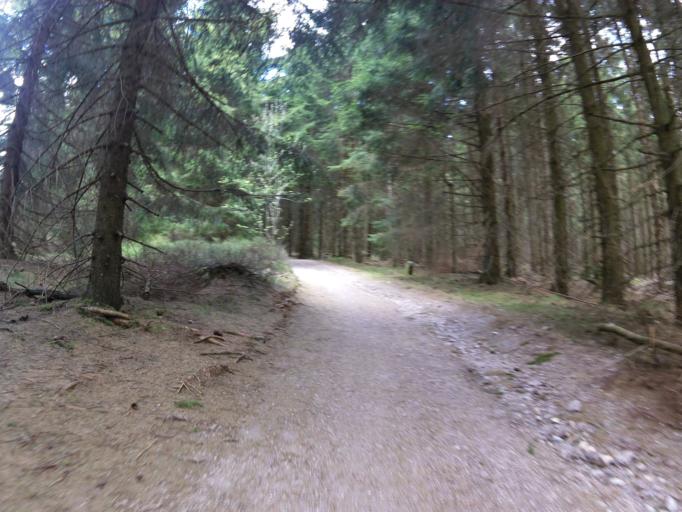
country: DE
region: Thuringia
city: Oberhof
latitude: 50.7051
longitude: 10.6973
